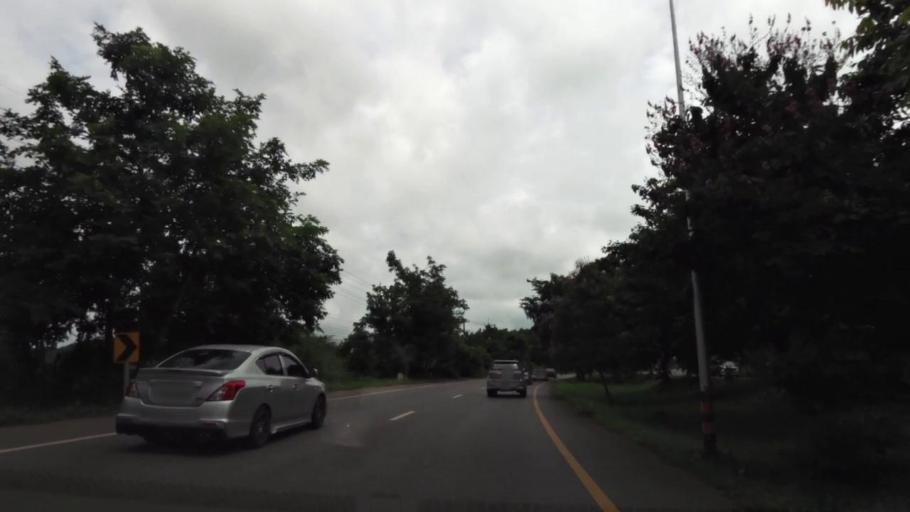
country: TH
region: Chanthaburi
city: Na Yai Am
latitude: 12.7394
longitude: 101.8918
